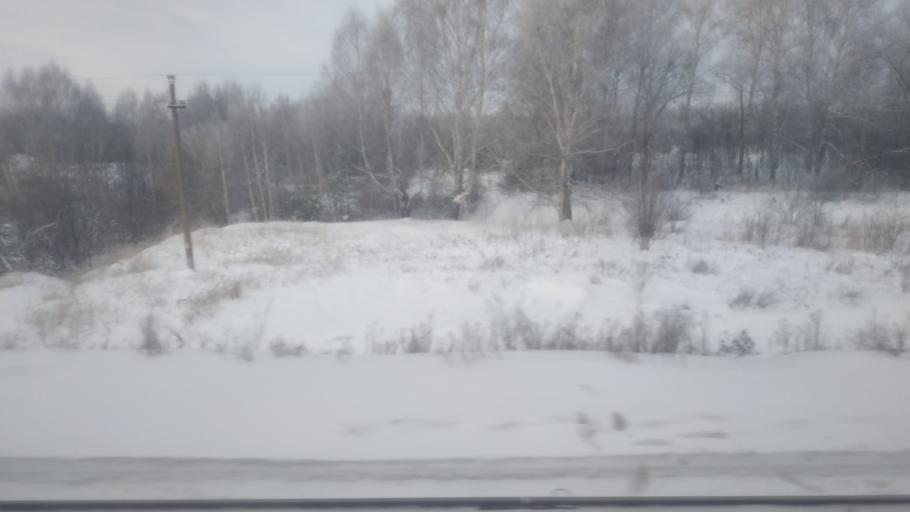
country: RU
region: Udmurtiya
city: Kizner
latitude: 56.3894
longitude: 51.7229
